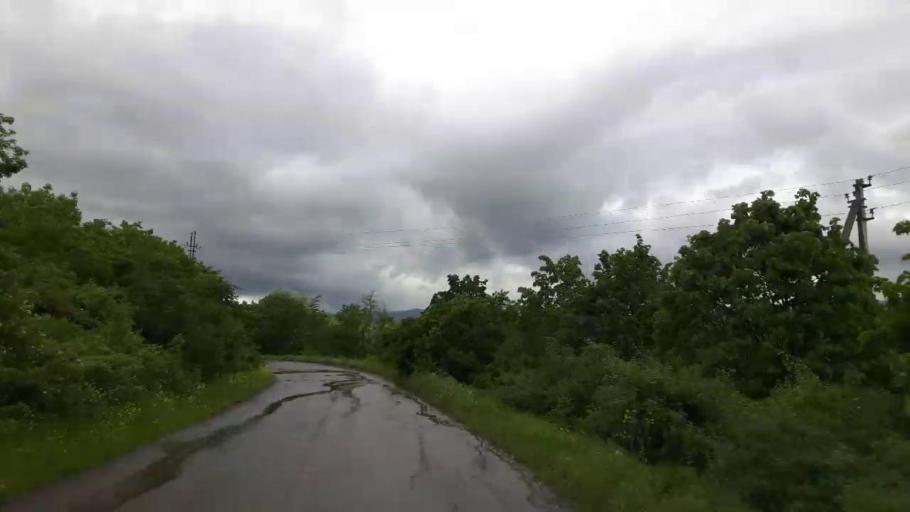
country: GE
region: Shida Kartli
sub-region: Khashuris Raioni
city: Khashuri
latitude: 41.9844
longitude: 43.6771
